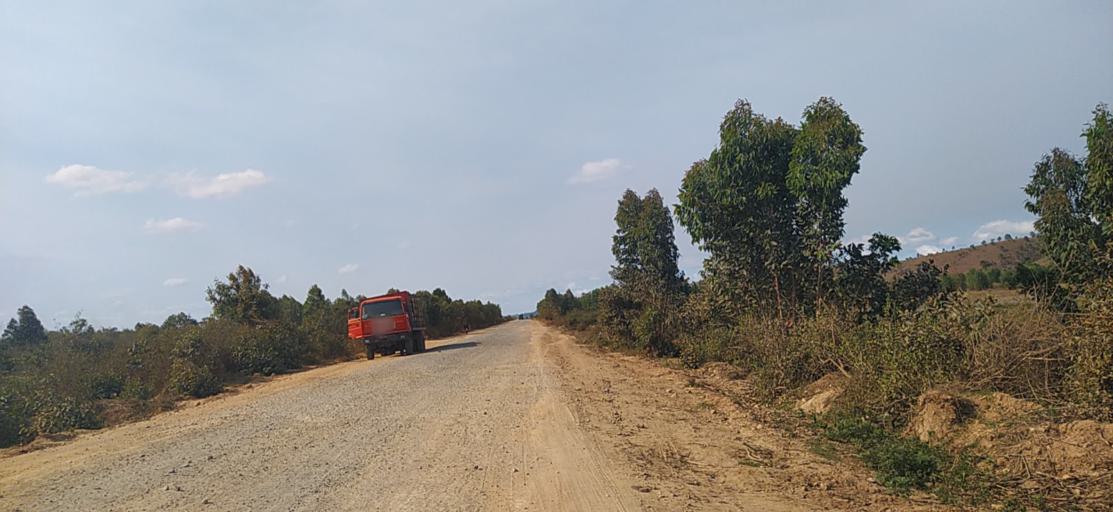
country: MG
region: Alaotra Mangoro
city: Moramanga
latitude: -18.6833
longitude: 48.2718
